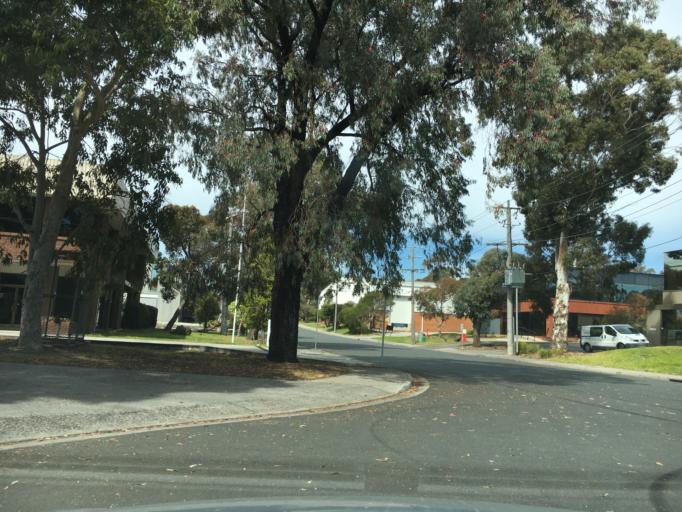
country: AU
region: Victoria
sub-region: Monash
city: Chadstone
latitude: -37.8932
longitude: 145.0989
